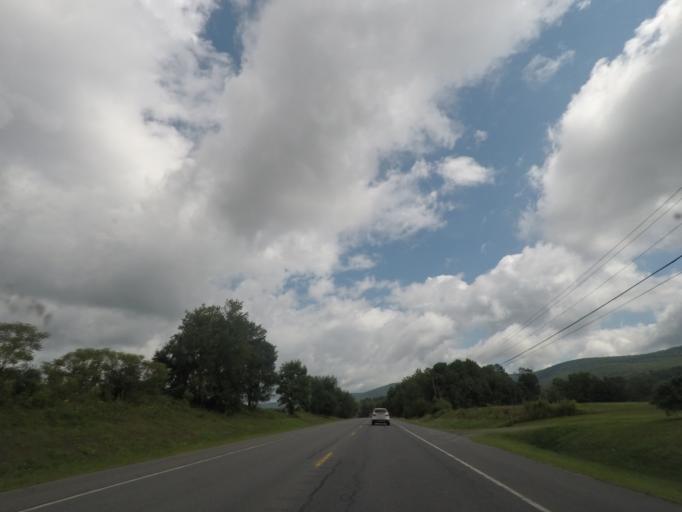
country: US
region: Massachusetts
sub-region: Berkshire County
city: Lanesborough
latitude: 42.5619
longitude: -73.3715
